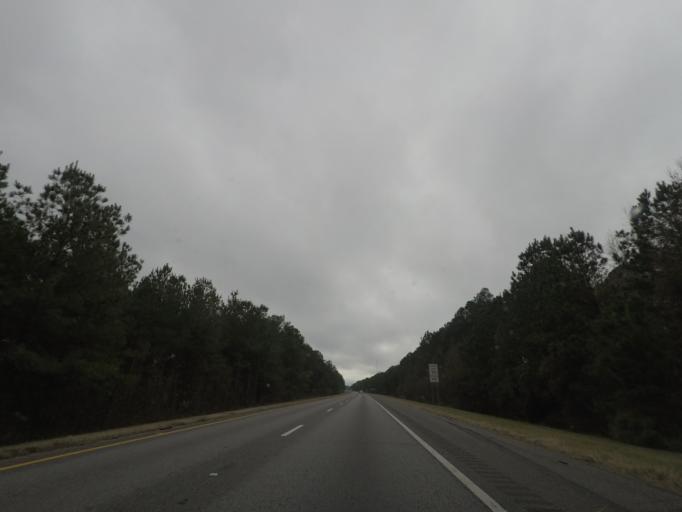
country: US
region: South Carolina
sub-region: Orangeburg County
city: Holly Hill
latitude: 33.3711
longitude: -80.5236
